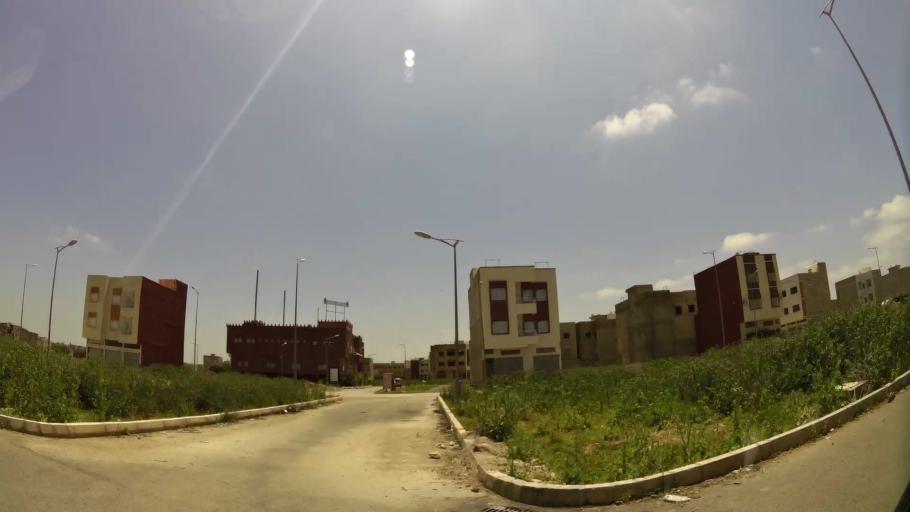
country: MA
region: Fes-Boulemane
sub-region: Fes
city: Fes
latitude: 34.0369
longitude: -5.0545
